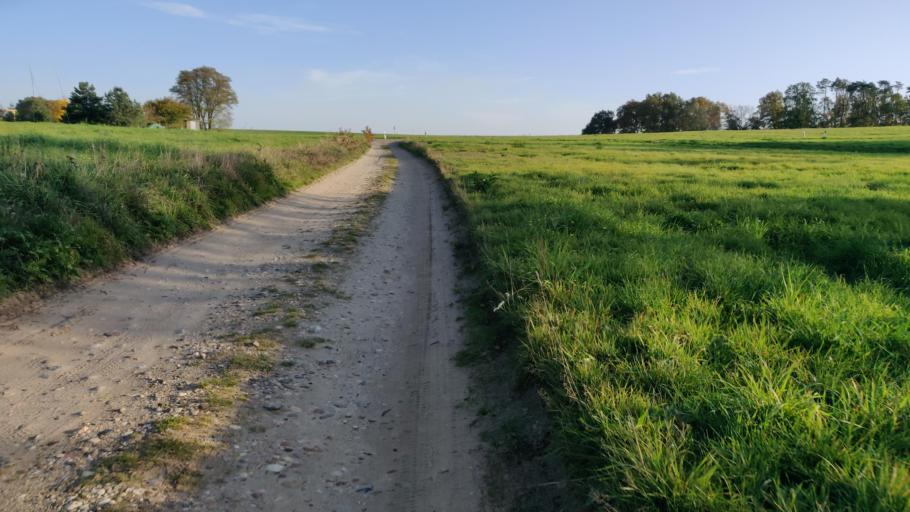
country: DE
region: Brandenburg
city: Ortrand
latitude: 51.3690
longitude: 13.7502
